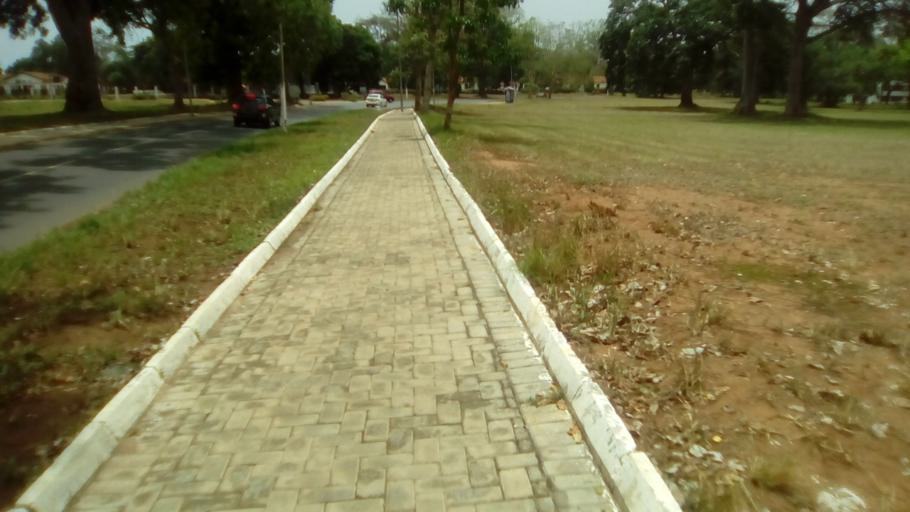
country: GH
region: Greater Accra
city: Medina Estates
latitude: 5.6447
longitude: -0.1892
